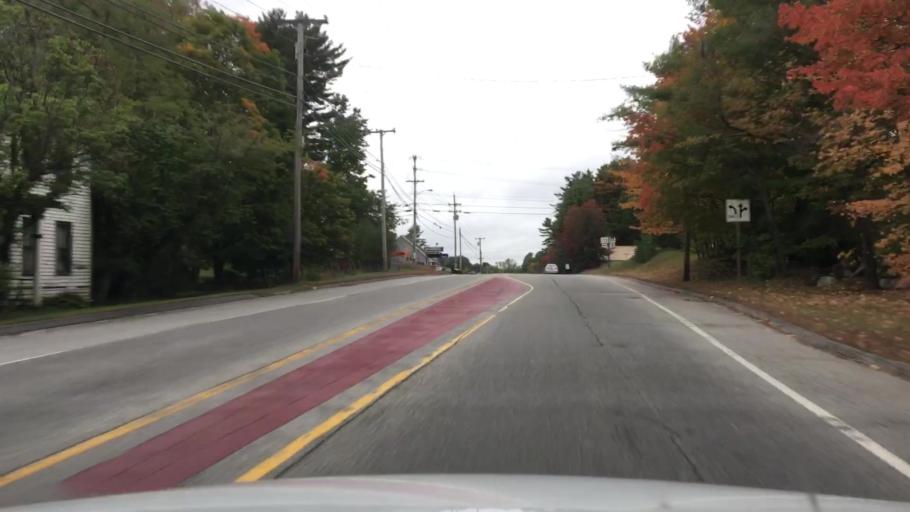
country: US
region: Maine
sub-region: Oxford County
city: Oxford
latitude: 44.1380
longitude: -70.4697
